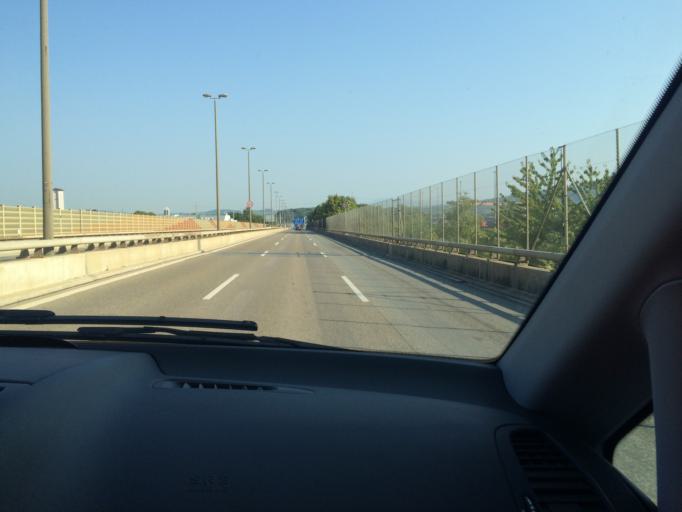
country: DE
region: Baden-Wuerttemberg
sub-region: Freiburg Region
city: Weil am Rhein
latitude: 47.5869
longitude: 7.6024
